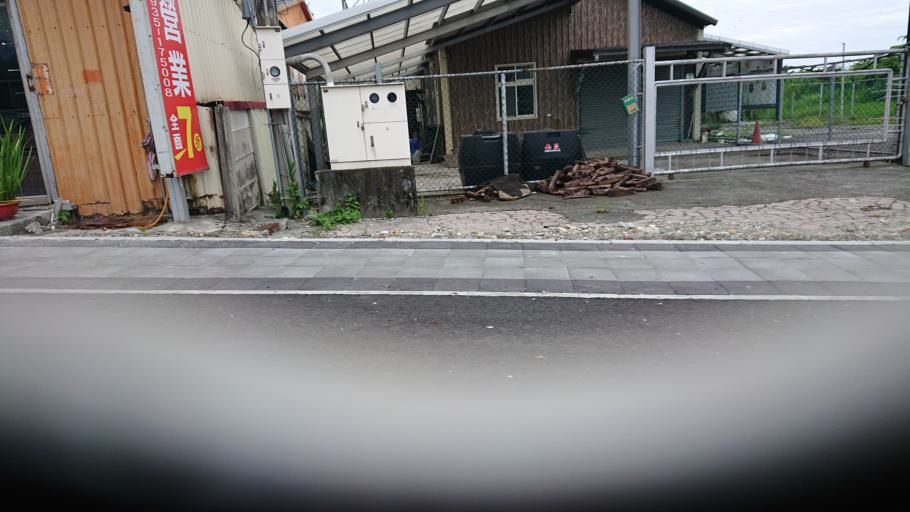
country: TW
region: Taiwan
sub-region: Hualien
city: Hualian
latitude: 23.9627
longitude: 121.6051
